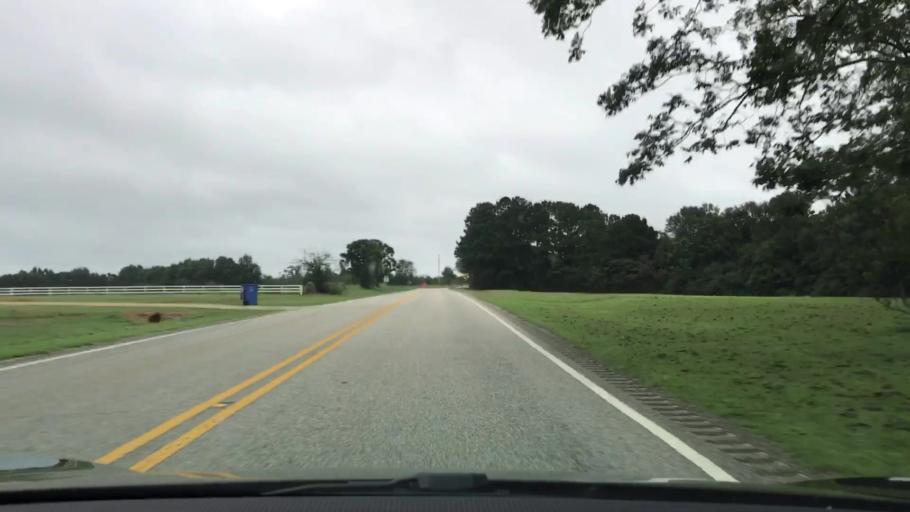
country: US
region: Alabama
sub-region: Coffee County
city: Elba
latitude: 31.3505
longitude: -86.1289
